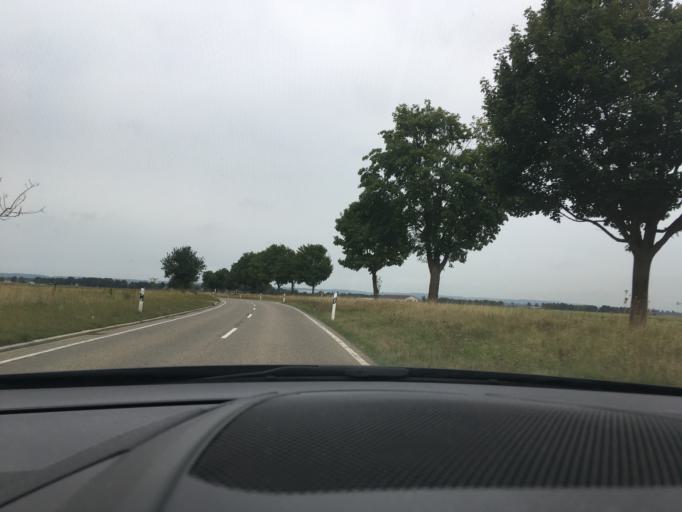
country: DE
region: Baden-Wuerttemberg
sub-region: Tuebingen Region
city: Kirchdorf
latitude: 48.0794
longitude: 10.1045
